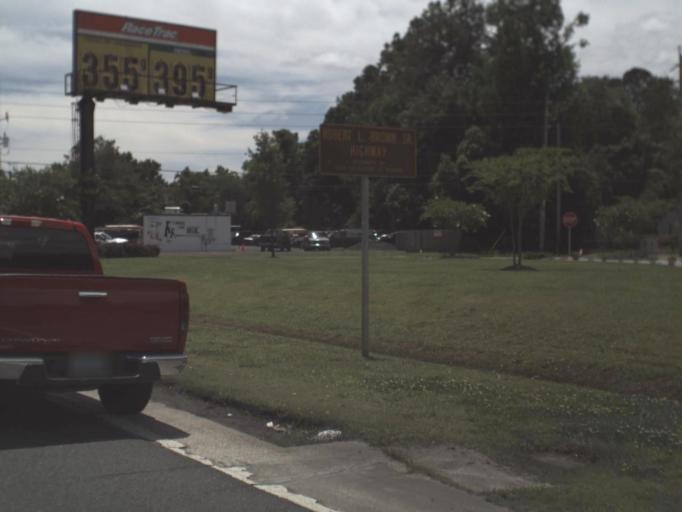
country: US
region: Florida
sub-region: Nassau County
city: Nassau Village-Ratliff
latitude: 30.4166
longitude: -81.7503
